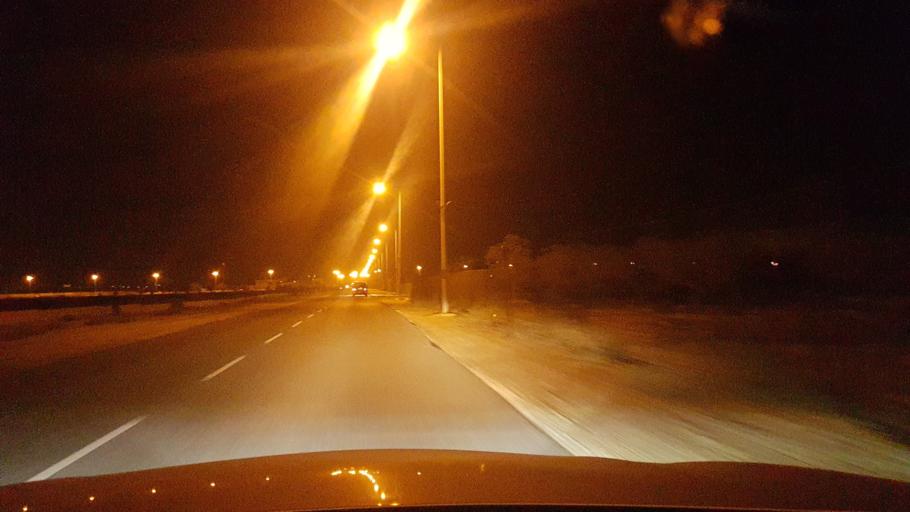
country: BH
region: Central Governorate
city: Dar Kulayb
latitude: 26.0212
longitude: 50.4821
